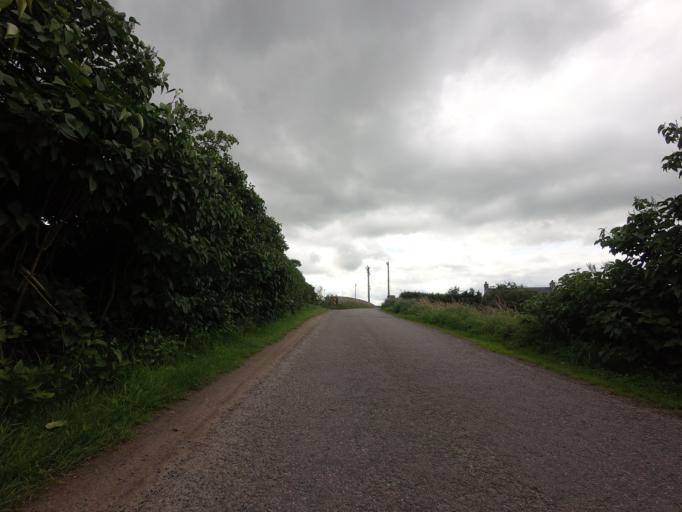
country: GB
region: Scotland
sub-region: Moray
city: Kinloss
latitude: 57.6355
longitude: -3.5182
